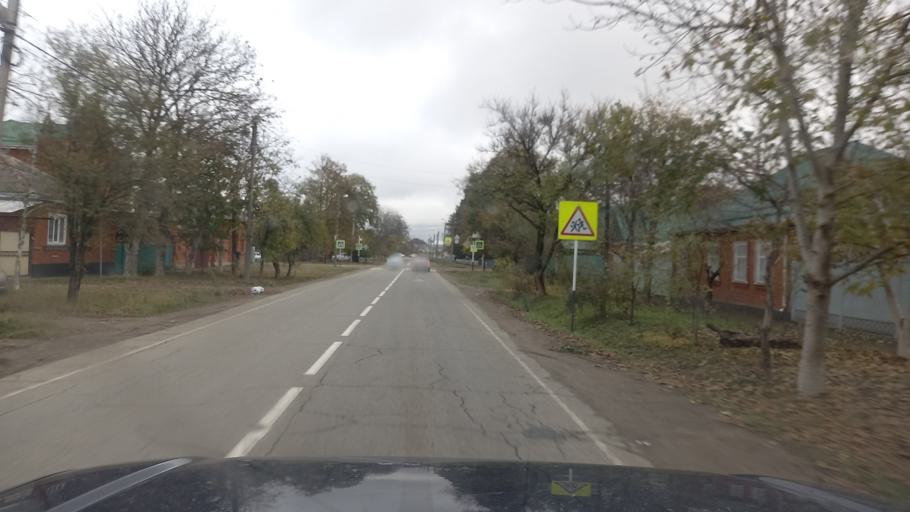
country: RU
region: Adygeya
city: Maykop
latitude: 44.6074
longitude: 40.0753
